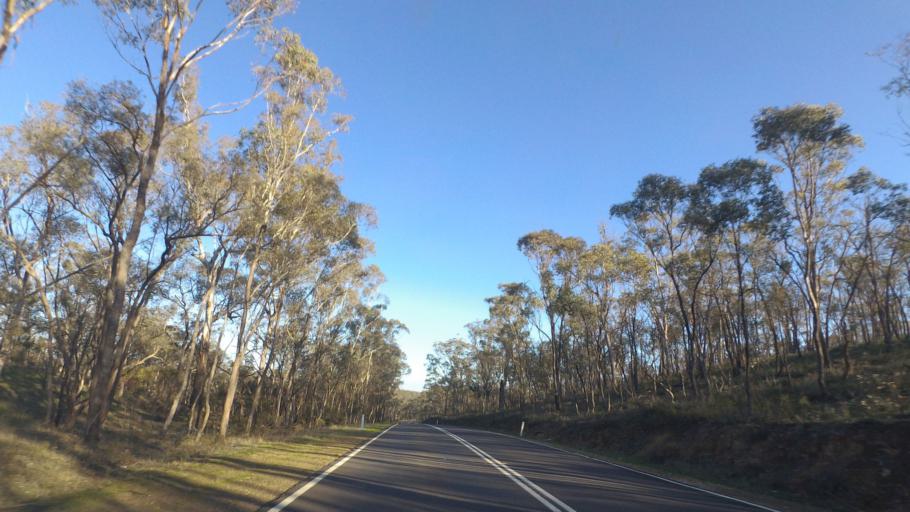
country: AU
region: Victoria
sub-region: Greater Bendigo
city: Kennington
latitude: -36.9130
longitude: 144.4926
